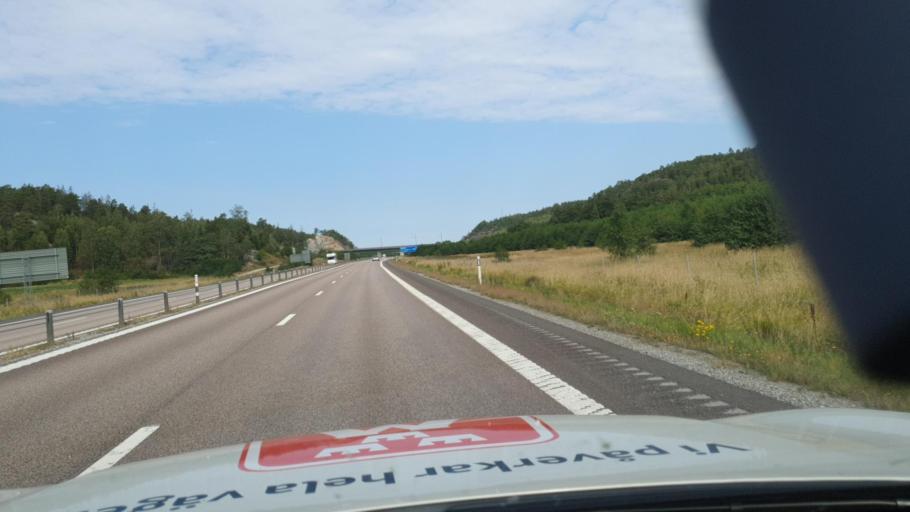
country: SE
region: Vaestra Goetaland
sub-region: Stromstads Kommun
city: Stroemstad
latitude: 58.9247
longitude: 11.2563
